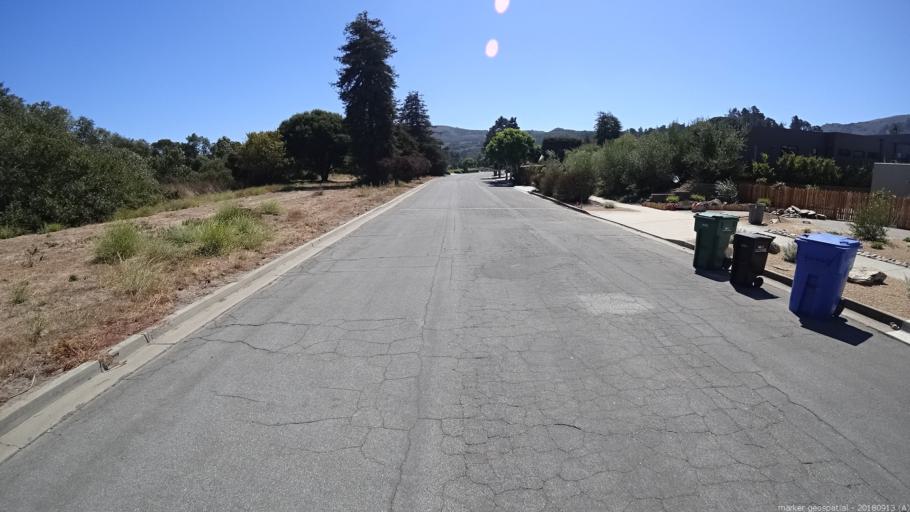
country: US
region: California
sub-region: Monterey County
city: Carmel-by-the-Sea
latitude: 36.5352
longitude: -121.8651
